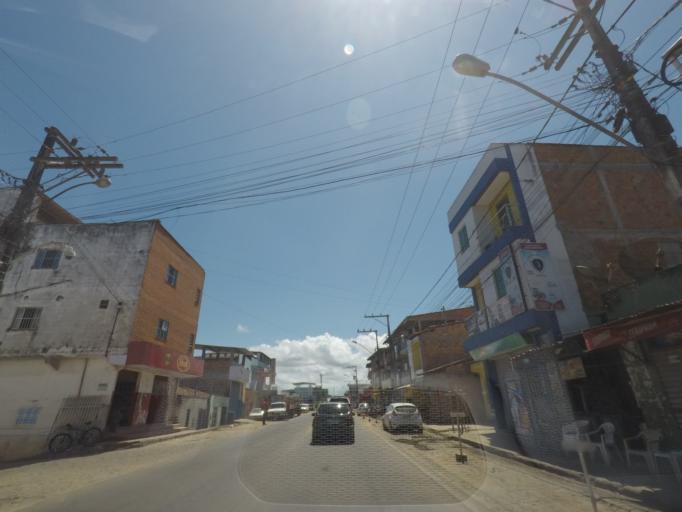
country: BR
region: Bahia
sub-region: Valenca
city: Valenca
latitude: -13.3572
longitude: -39.0640
